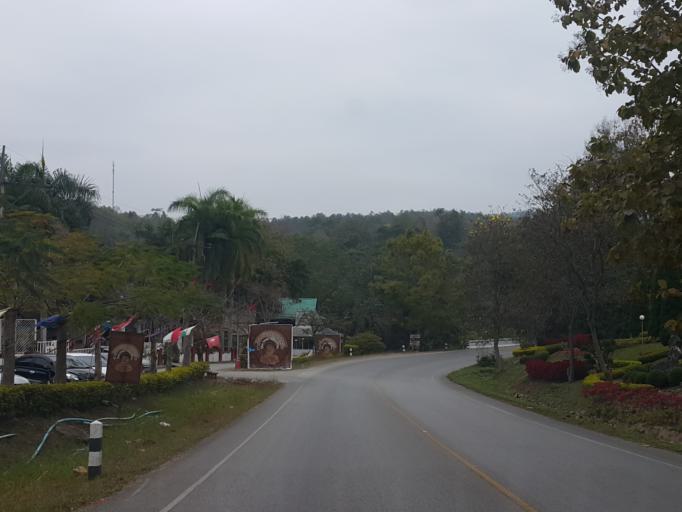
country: TH
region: Chiang Mai
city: Hang Dong
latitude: 18.7767
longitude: 98.8538
